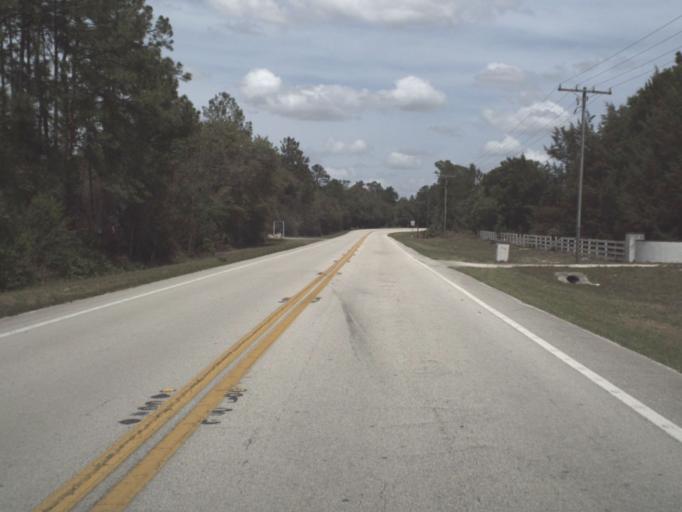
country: US
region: Florida
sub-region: Lake County
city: Lake Mack-Forest Hills
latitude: 28.9274
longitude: -81.4408
